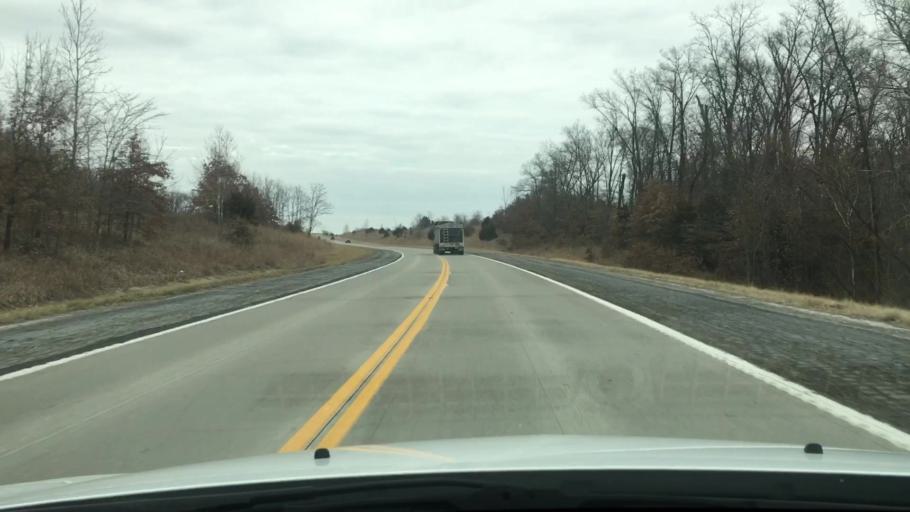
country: US
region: Missouri
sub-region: Audrain County
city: Mexico
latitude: 39.1473
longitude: -91.8442
